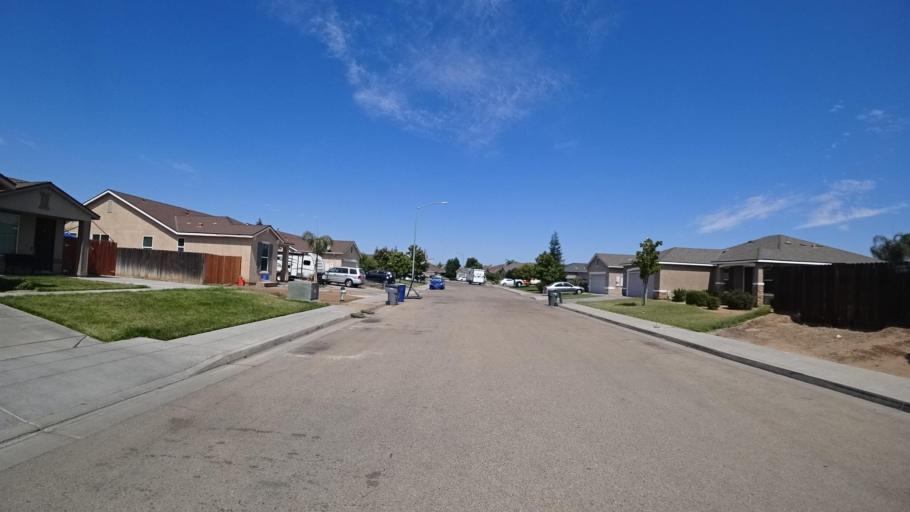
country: US
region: California
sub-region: Fresno County
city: Sunnyside
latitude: 36.7185
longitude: -119.7111
